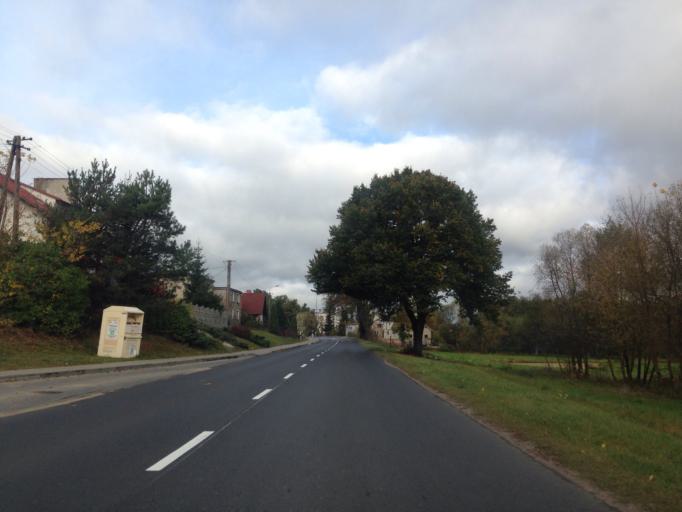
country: PL
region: Kujawsko-Pomorskie
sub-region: Powiat brodnicki
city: Bartniczka
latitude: 53.2497
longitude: 19.6056
